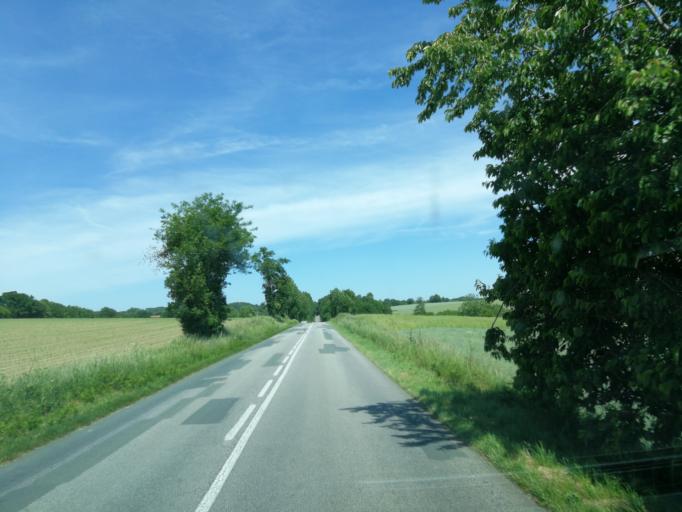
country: FR
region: Poitou-Charentes
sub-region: Departement des Deux-Sevres
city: Courlay
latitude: 46.7923
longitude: -0.6024
